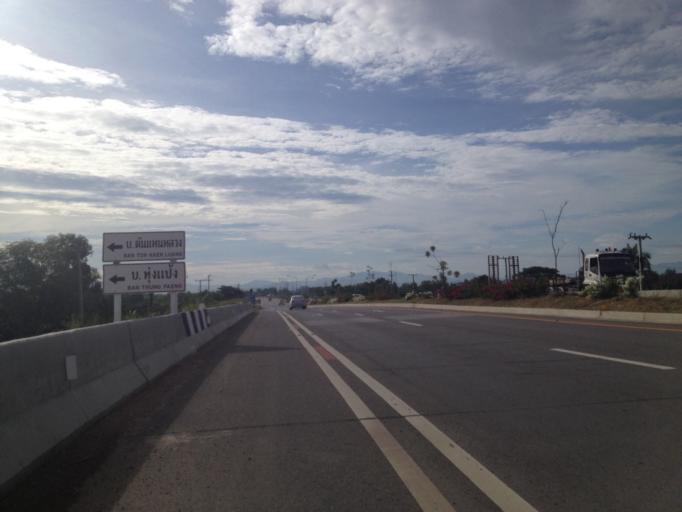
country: TH
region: Lamphun
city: Pa Sang
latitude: 18.5358
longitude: 98.8587
